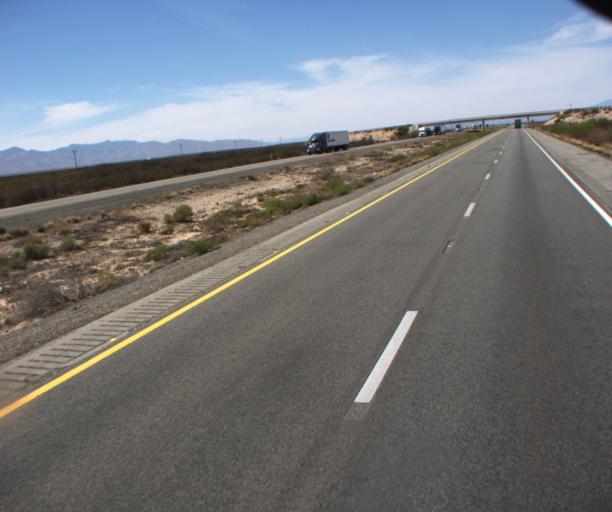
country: US
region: New Mexico
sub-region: Hidalgo County
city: Lordsburg
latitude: 32.2704
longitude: -109.2461
